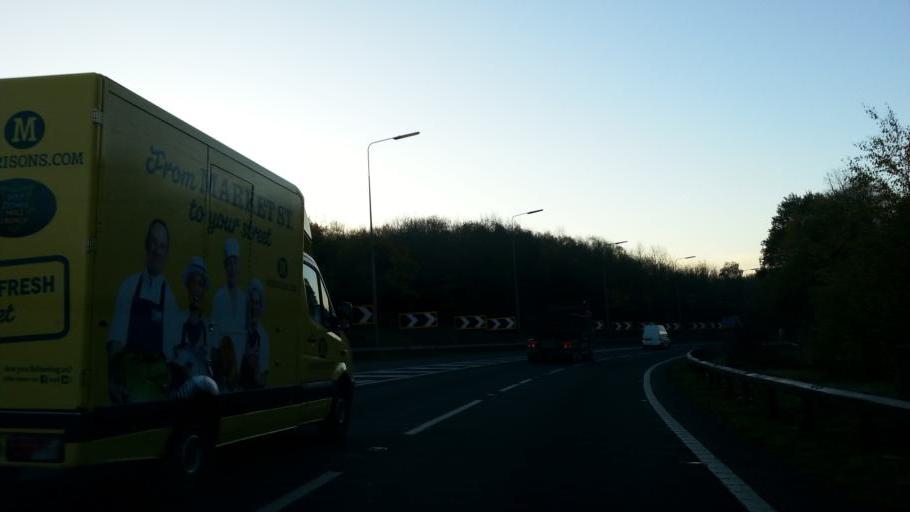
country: GB
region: England
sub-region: Hertfordshire
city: Abbots Langley
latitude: 51.7185
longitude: -0.3845
